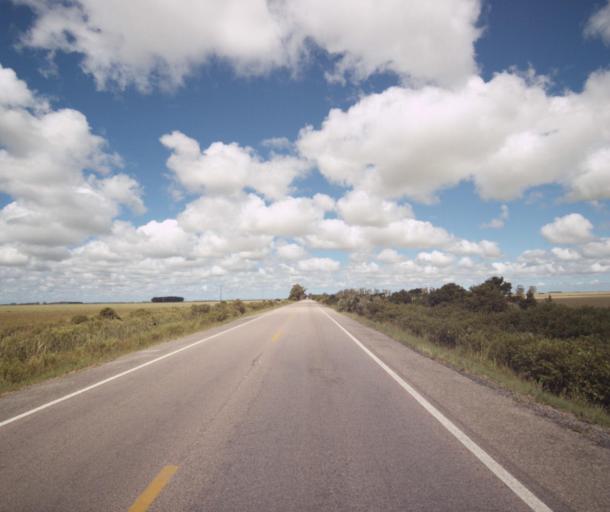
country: BR
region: Rio Grande do Sul
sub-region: Rio Grande
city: Rio Grande
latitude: -32.1757
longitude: -52.4178
